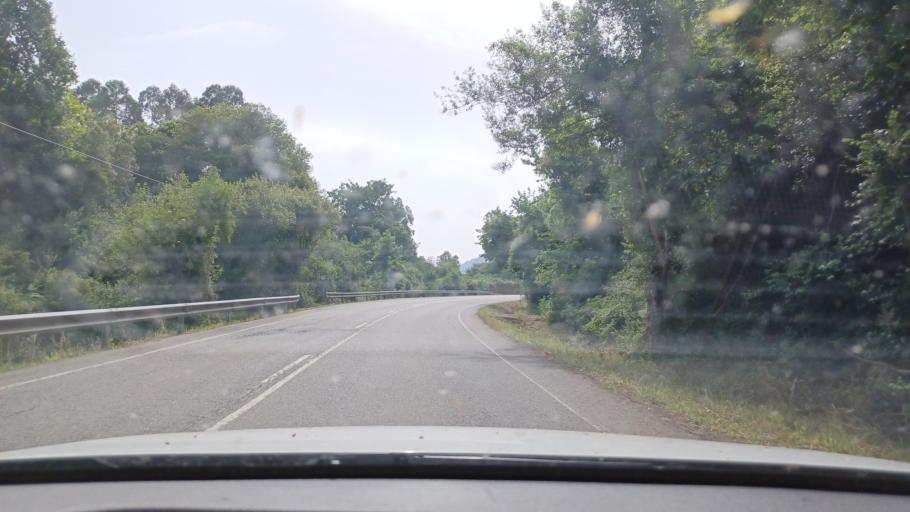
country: ES
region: Asturias
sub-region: Province of Asturias
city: Ribadesella
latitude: 43.4431
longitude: -4.9986
